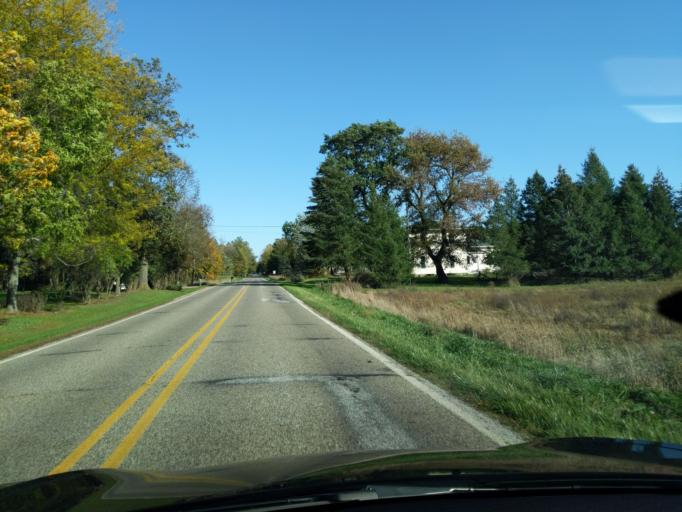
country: US
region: Michigan
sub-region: Shiawassee County
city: Laingsburg
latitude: 42.9290
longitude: -84.4520
